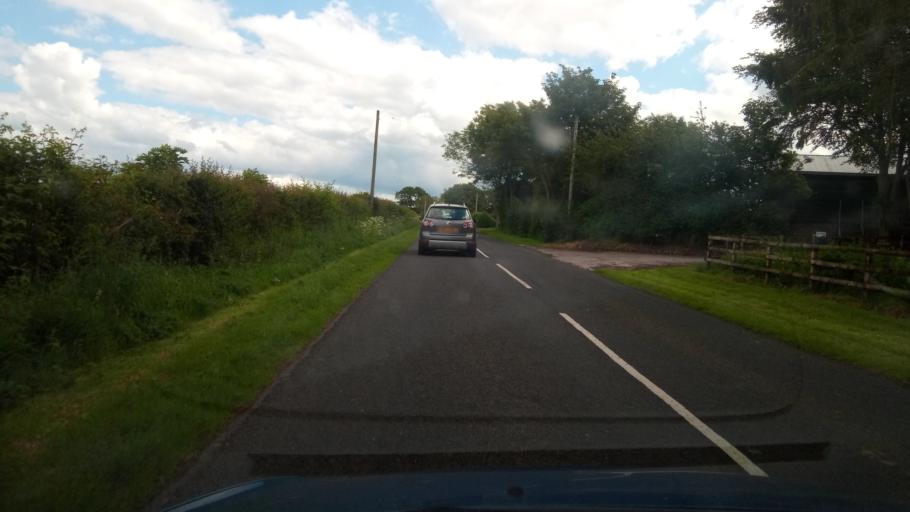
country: GB
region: Scotland
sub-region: The Scottish Borders
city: Coldstream
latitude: 55.6035
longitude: -2.2878
